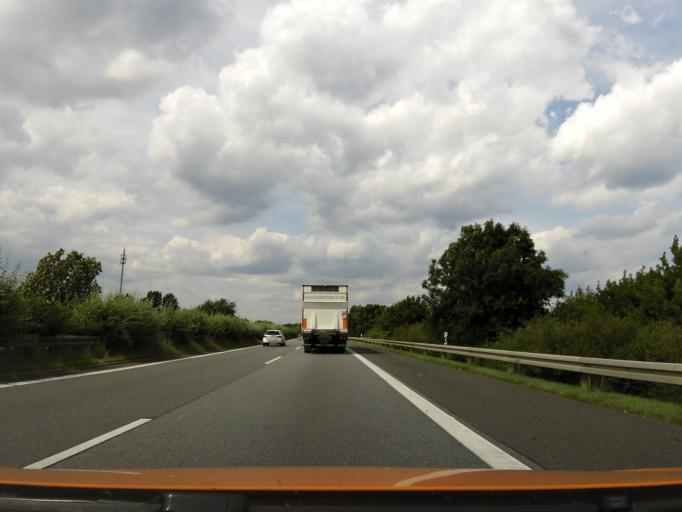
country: DE
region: Berlin
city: Blankenfelde
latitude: 52.6686
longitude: 13.4047
